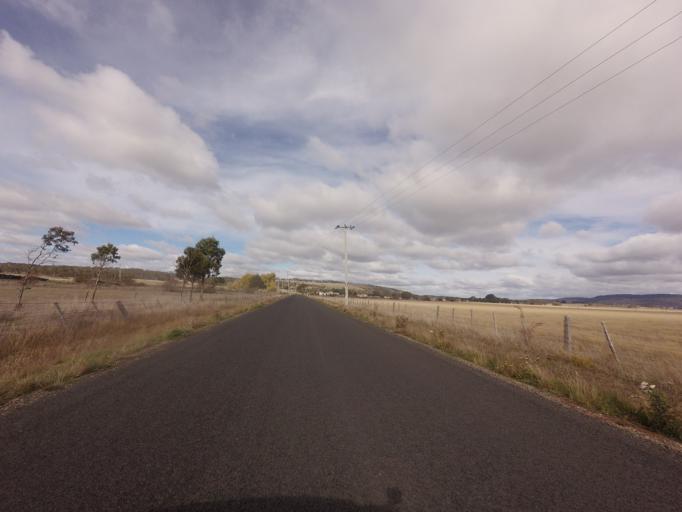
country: AU
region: Tasmania
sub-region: Brighton
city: Bridgewater
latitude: -42.4010
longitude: 147.3894
